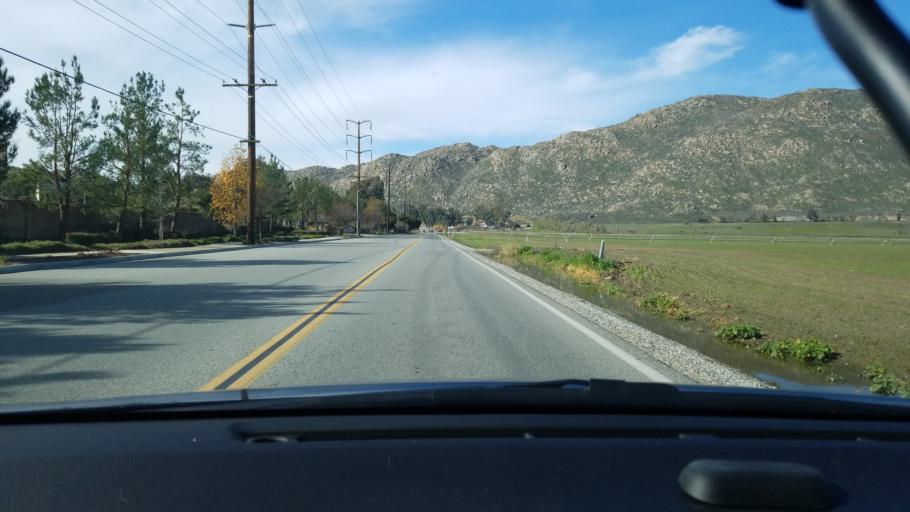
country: US
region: California
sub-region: Riverside County
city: Green Acres
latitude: 33.7729
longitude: -117.0277
